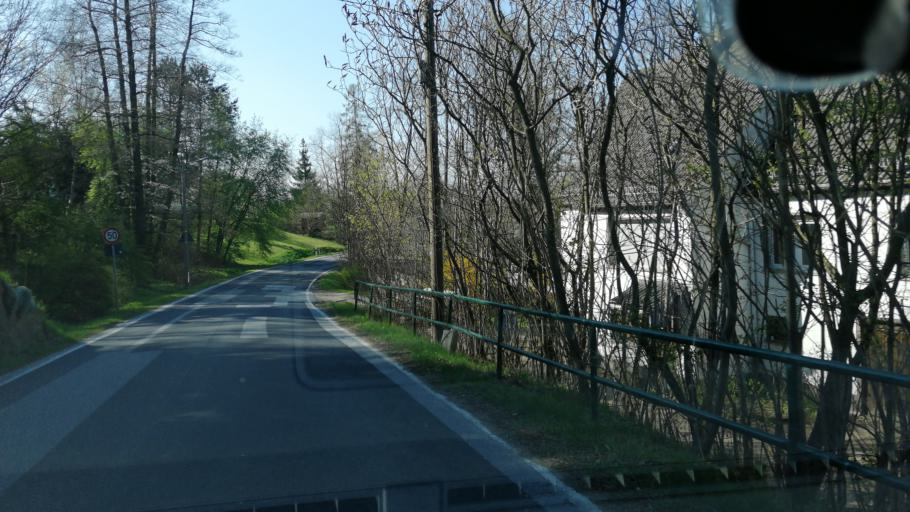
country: DE
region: Saxony
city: Goerlitz
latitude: 51.1801
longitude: 14.9349
